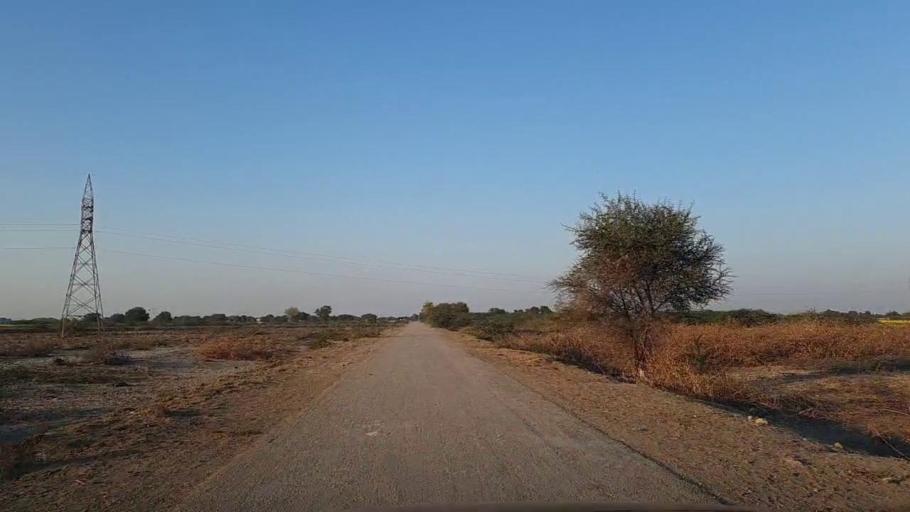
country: PK
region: Sindh
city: Nawabshah
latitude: 26.2204
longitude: 68.3379
